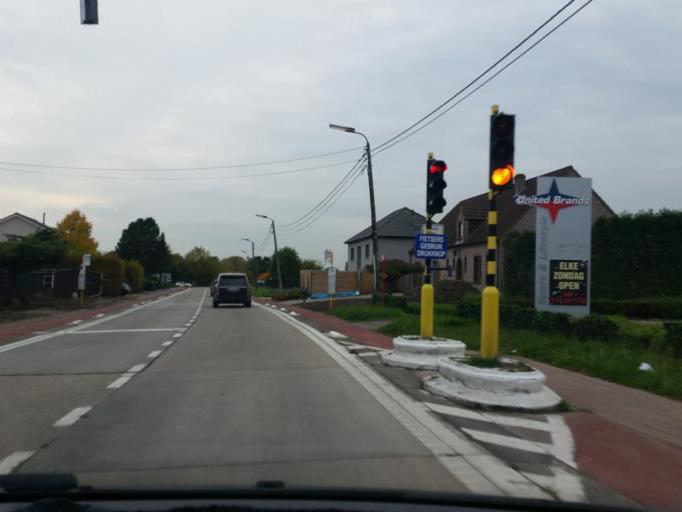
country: BE
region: Flanders
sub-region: Provincie Antwerpen
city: Sint-Katelijne-Waver
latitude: 51.0642
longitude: 4.5584
